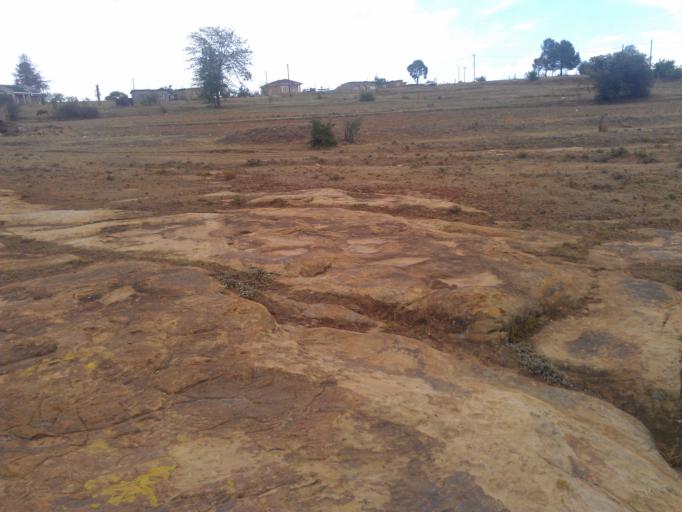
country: ZA
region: Orange Free State
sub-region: Thabo Mofutsanyana District Municipality
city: Ficksburg
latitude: -28.9621
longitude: 27.7449
